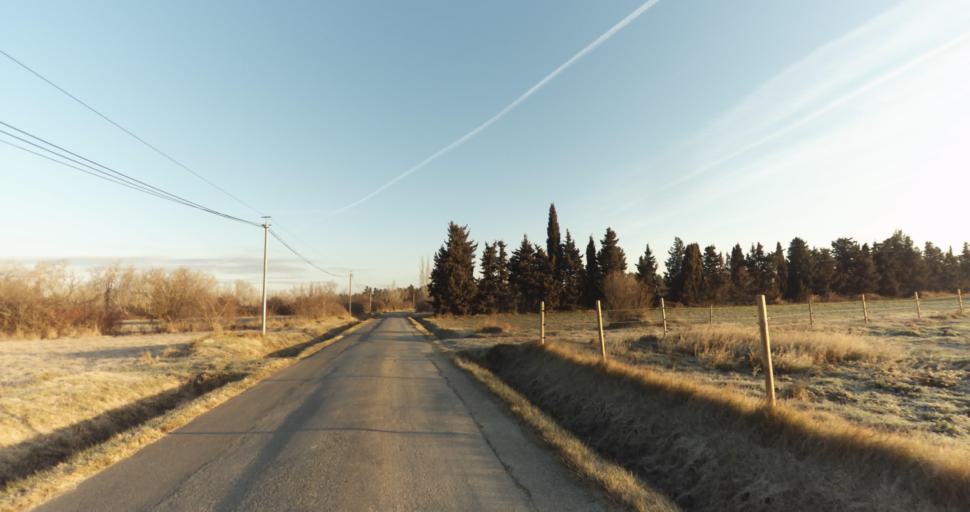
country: FR
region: Provence-Alpes-Cote d'Azur
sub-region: Departement des Bouches-du-Rhone
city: Barbentane
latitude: 43.8919
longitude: 4.7716
